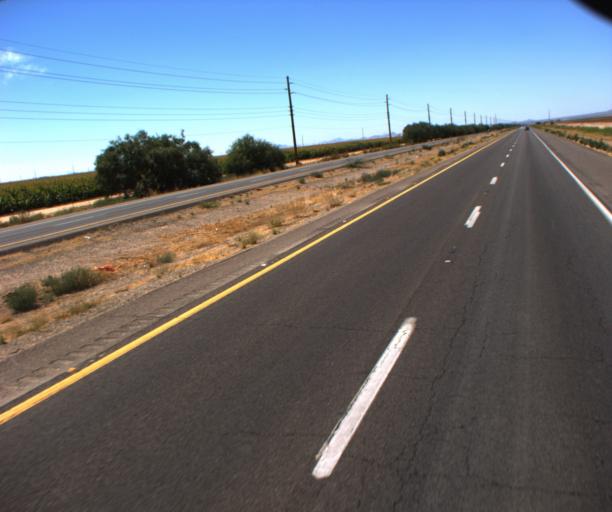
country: US
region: Arizona
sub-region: Pinal County
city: Maricopa
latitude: 32.9842
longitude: -112.0480
